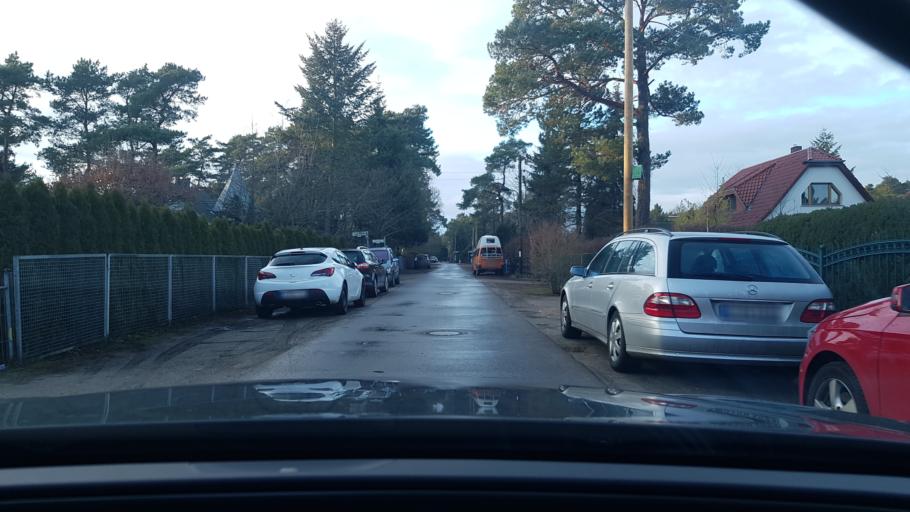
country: DE
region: Berlin
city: Muggelheim
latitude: 52.4191
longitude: 13.6699
